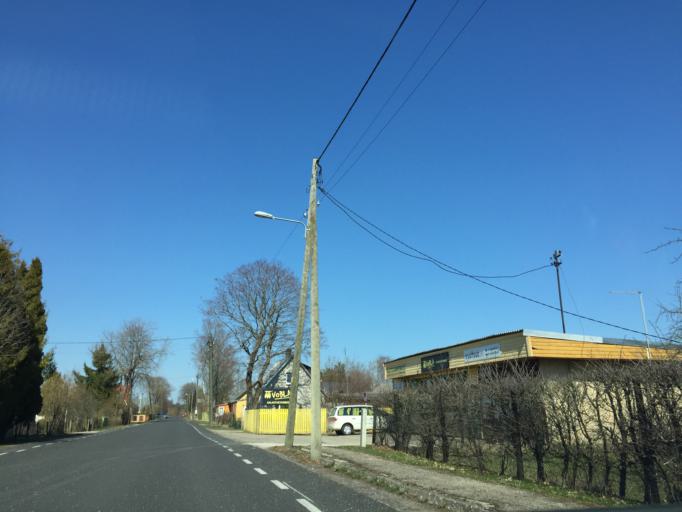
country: EE
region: Jogevamaa
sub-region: Mustvee linn
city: Mustvee
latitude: 58.8578
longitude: 26.9508
